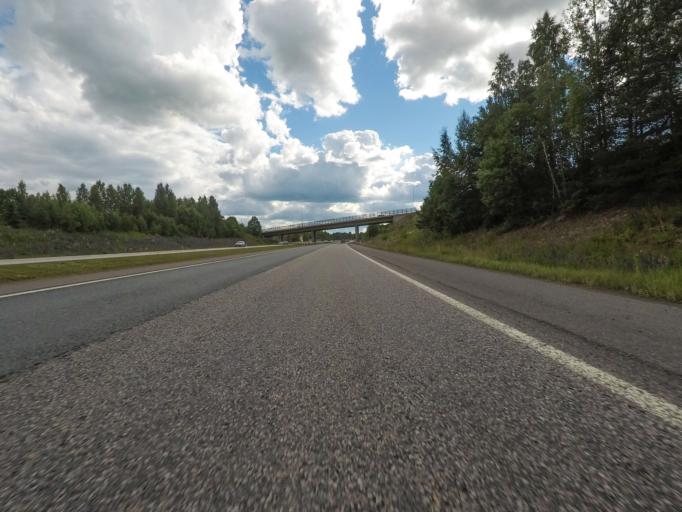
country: FI
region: Uusimaa
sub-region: Helsinki
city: Maentsaelae
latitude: 60.6465
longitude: 25.3082
